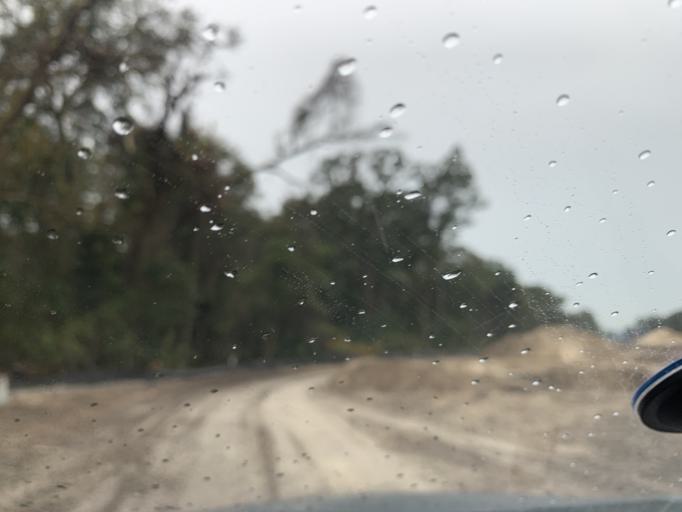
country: US
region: Florida
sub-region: Hernando County
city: Masaryktown
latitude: 28.4517
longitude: -82.4541
